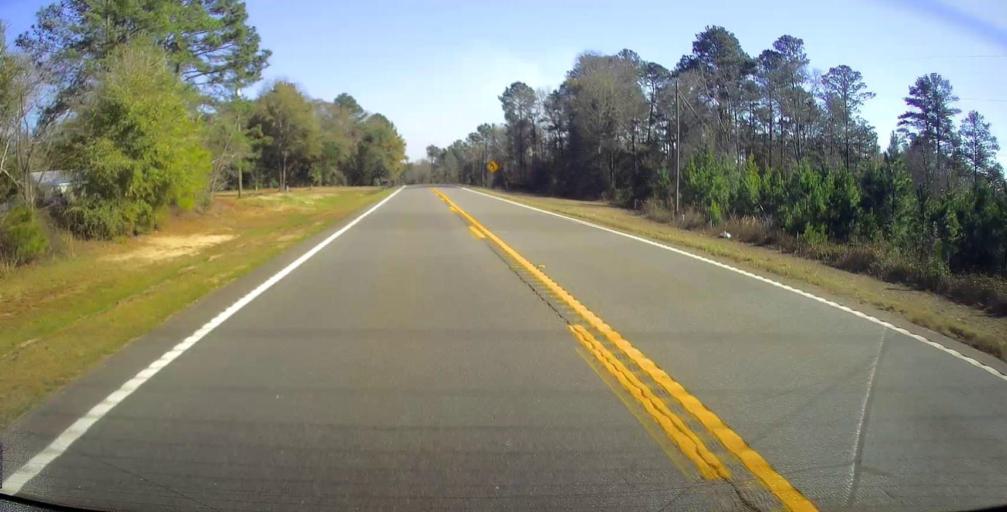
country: US
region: Georgia
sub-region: Macon County
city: Oglethorpe
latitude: 32.3546
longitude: -84.1745
